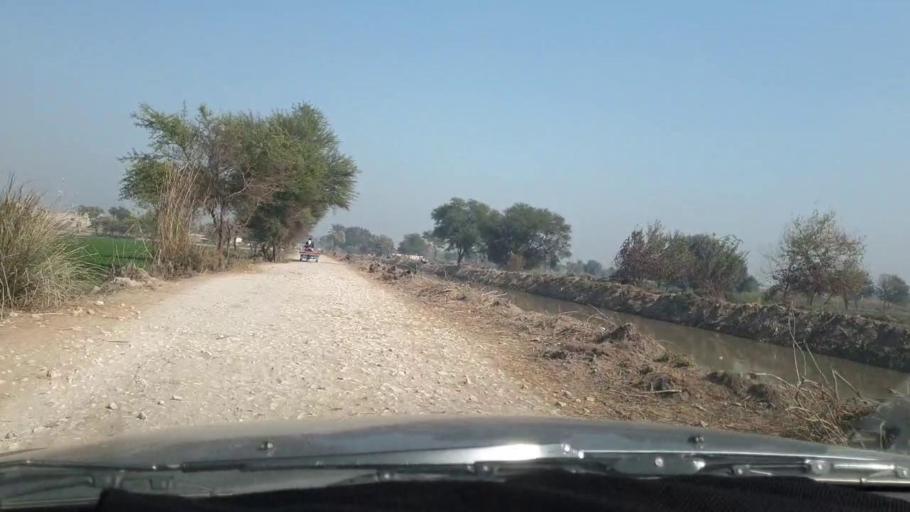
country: PK
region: Sindh
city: Khanpur
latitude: 27.8020
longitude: 69.5723
